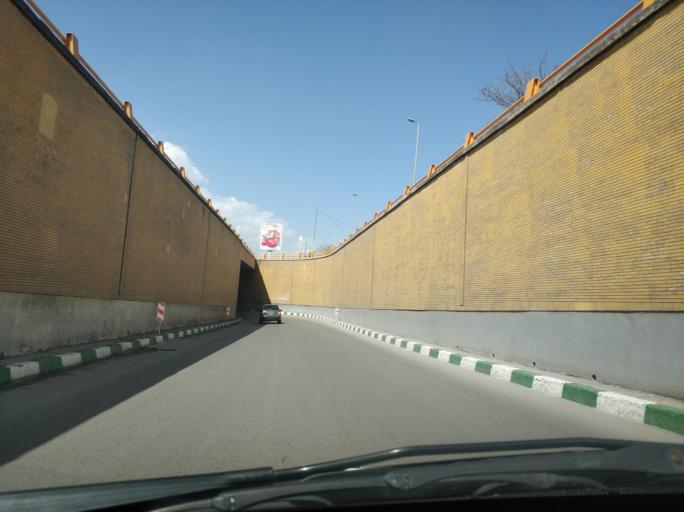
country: IR
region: Razavi Khorasan
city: Torqabeh
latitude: 36.3425
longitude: 59.4545
